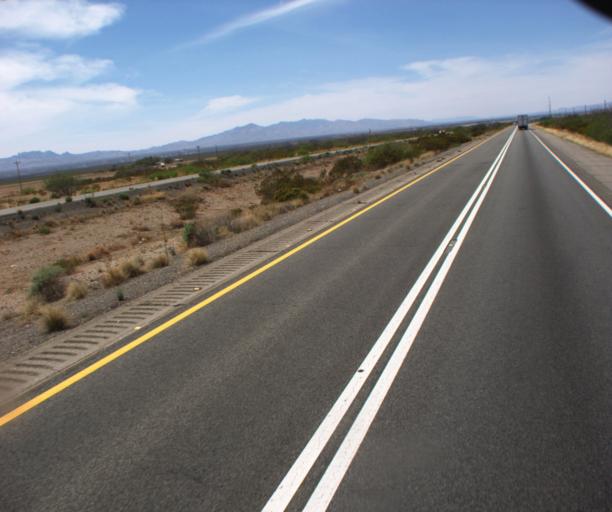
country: US
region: New Mexico
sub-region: Hidalgo County
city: Lordsburg
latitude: 32.2522
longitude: -109.1552
